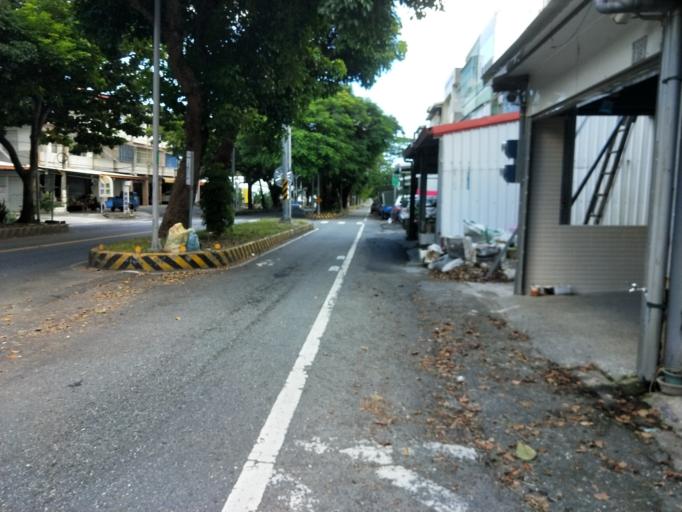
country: TW
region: Taiwan
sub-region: Taitung
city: Taitung
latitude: 22.7931
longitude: 121.1051
